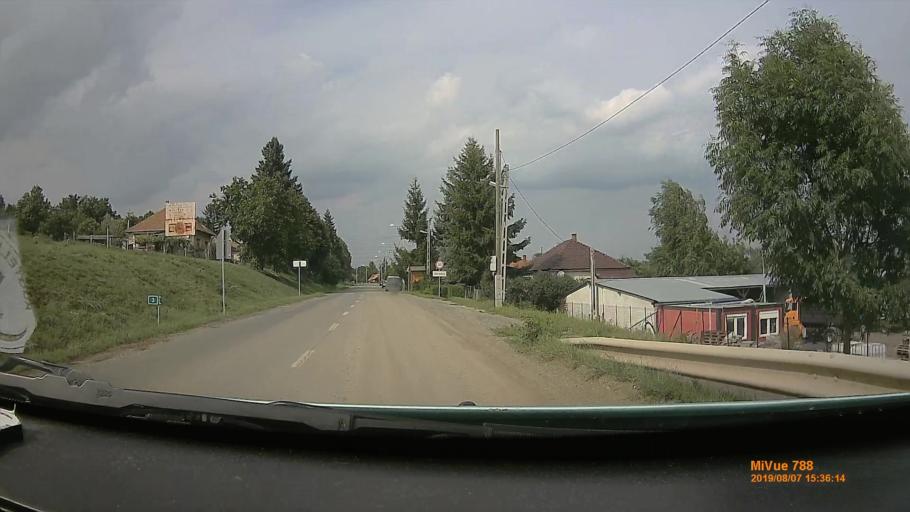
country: HU
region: Borsod-Abauj-Zemplen
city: Encs
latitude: 48.4107
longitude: 21.1732
